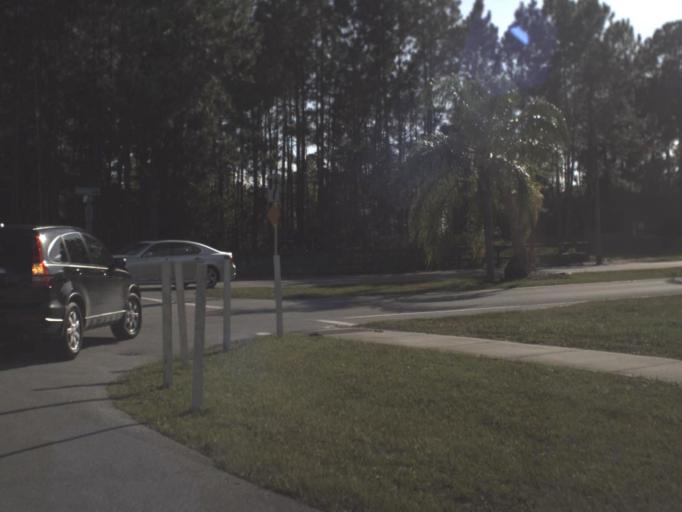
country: US
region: Florida
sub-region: Volusia County
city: Daytona Beach
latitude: 29.1974
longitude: -81.0858
